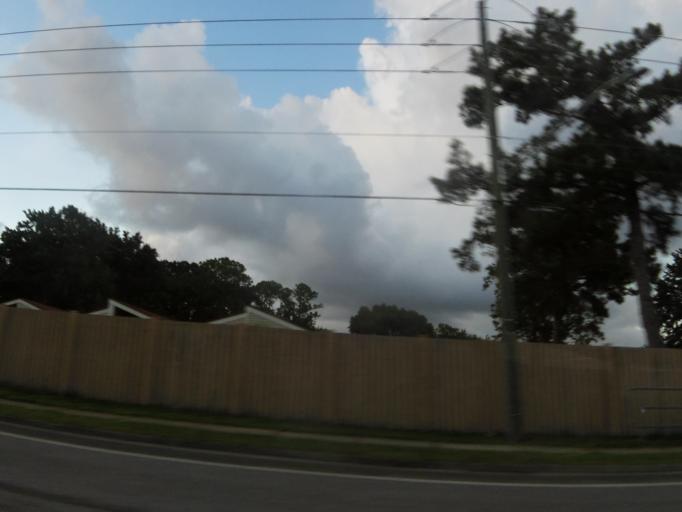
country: US
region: Florida
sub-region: Duval County
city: Jacksonville
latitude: 30.2324
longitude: -81.6011
